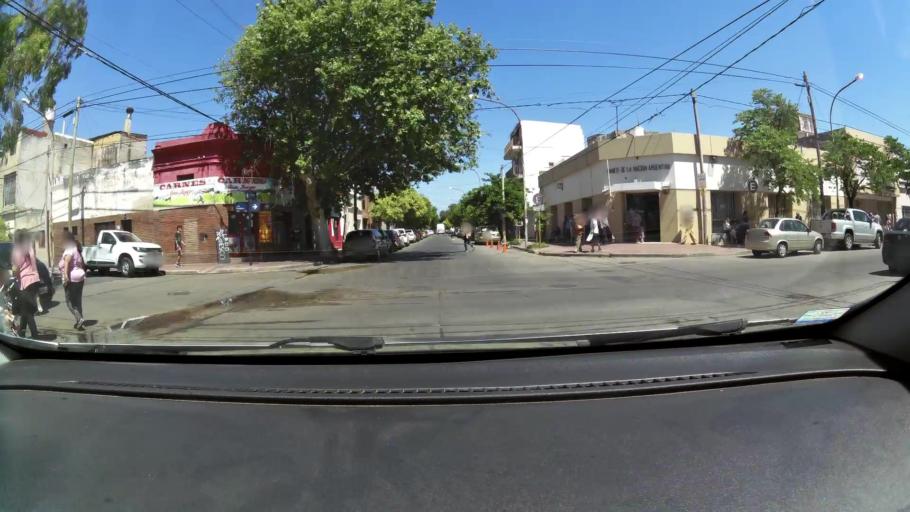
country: AR
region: Cordoba
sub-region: Departamento de Capital
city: Cordoba
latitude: -31.4244
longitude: -64.1494
